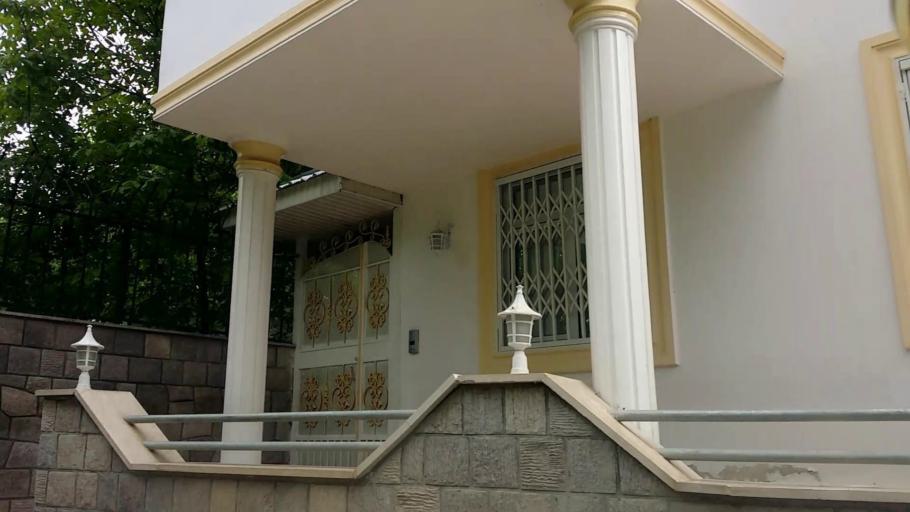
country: IR
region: Mazandaran
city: `Abbasabad
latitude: 36.4902
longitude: 51.1363
